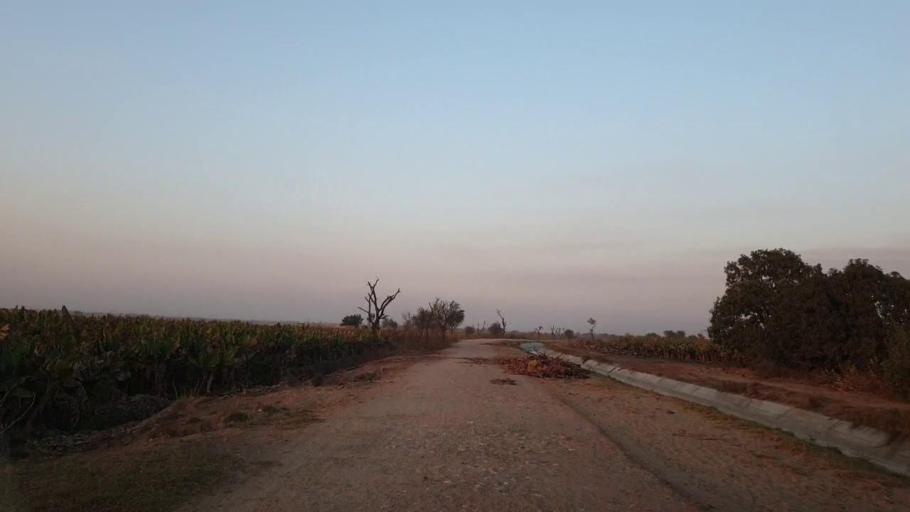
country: PK
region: Sindh
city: Berani
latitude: 25.6586
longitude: 68.7767
